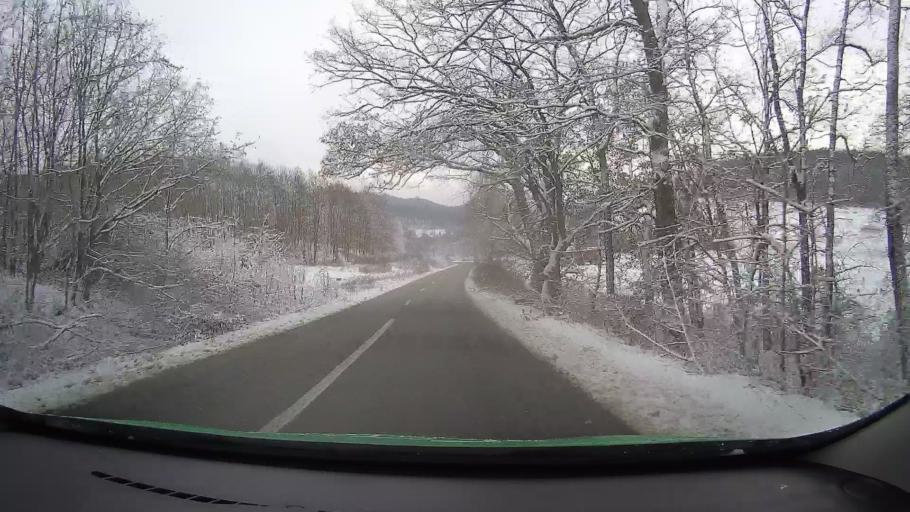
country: RO
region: Hunedoara
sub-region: Oras Hateg
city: Hateg
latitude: 45.6364
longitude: 22.9219
